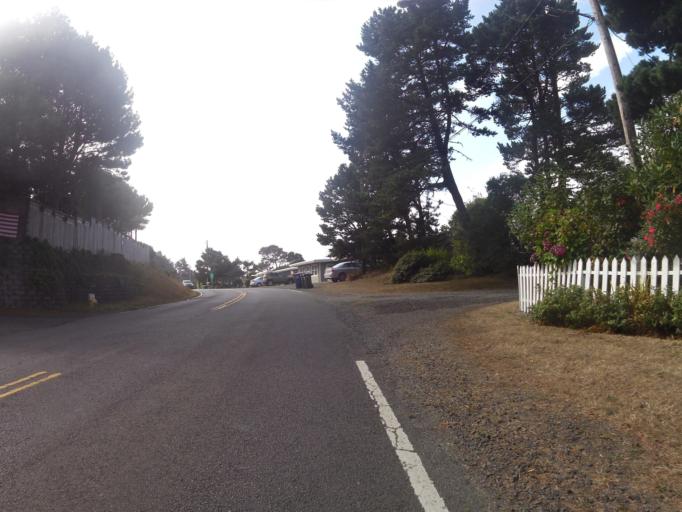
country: US
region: Oregon
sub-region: Lincoln County
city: Newport
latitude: 44.6492
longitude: -124.0573
